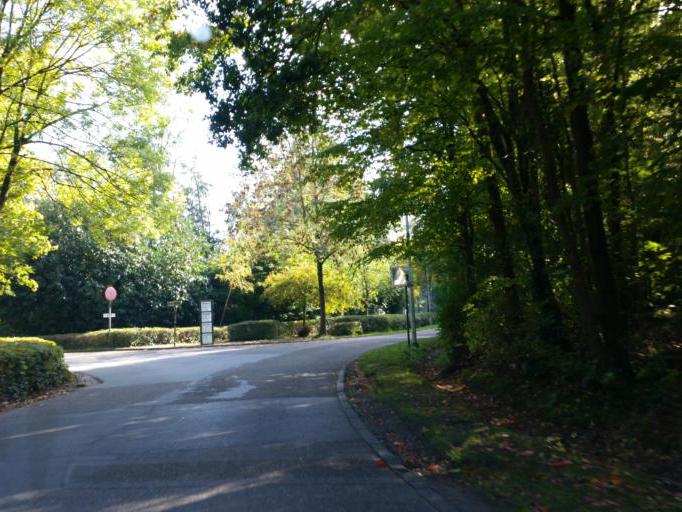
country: BE
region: Flanders
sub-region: Provincie Antwerpen
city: Aartselaar
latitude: 51.1618
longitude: 4.4032
